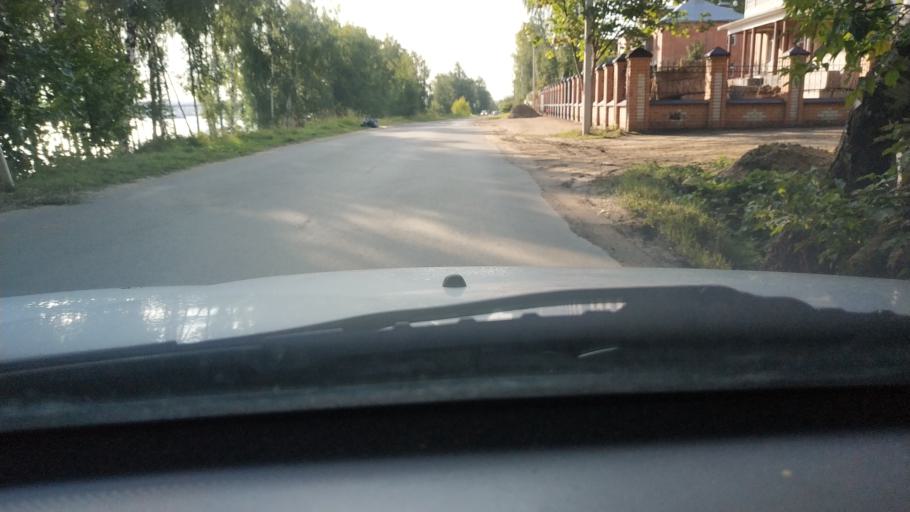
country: RU
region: Kostroma
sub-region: Kostromskoy Rayon
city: Kostroma
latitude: 57.7550
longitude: 40.9187
